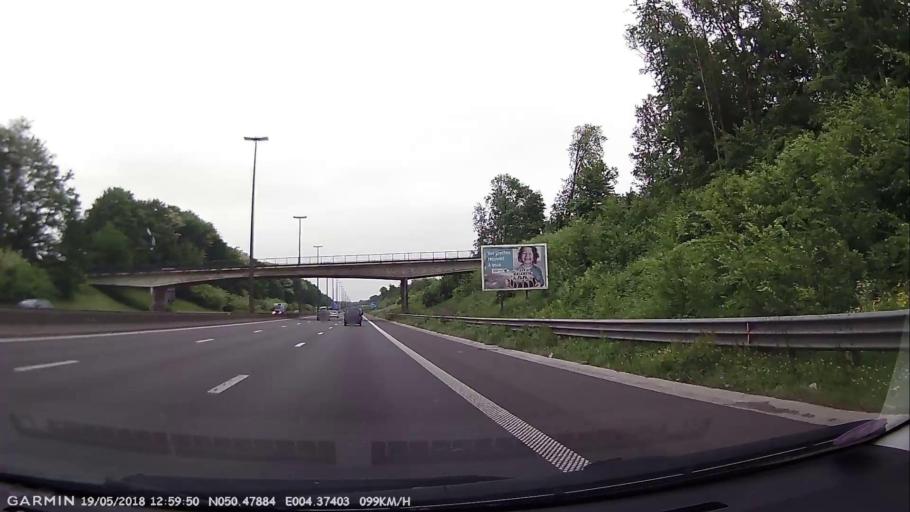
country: BE
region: Wallonia
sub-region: Province du Hainaut
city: Courcelles
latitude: 50.4788
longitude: 4.3744
